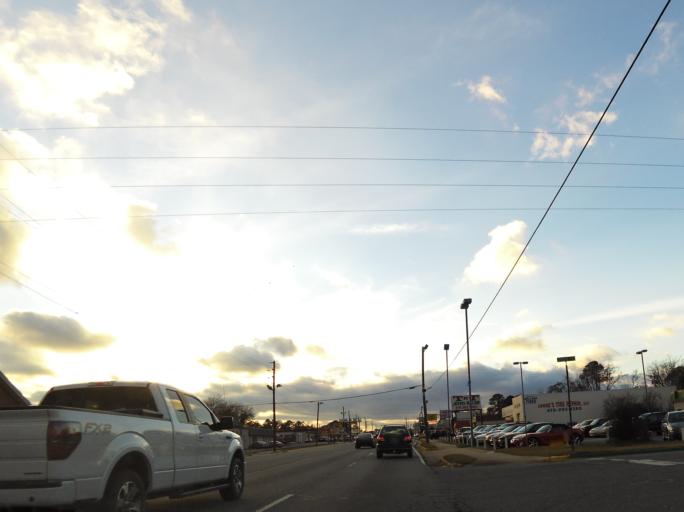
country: US
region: Georgia
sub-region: Houston County
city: Warner Robins
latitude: 32.6183
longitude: -83.6154
